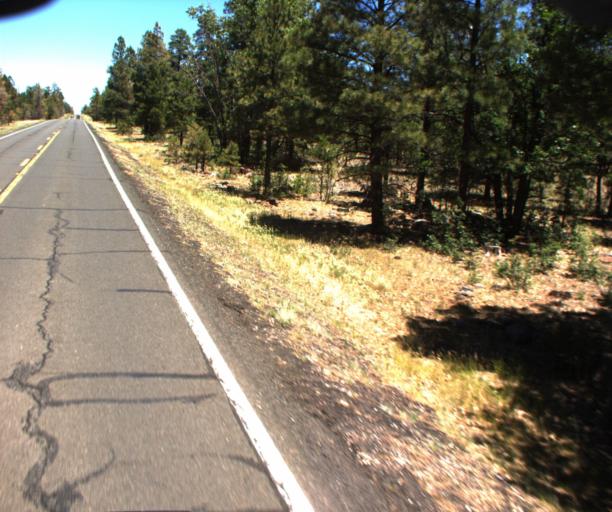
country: US
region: Arizona
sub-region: Gila County
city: Pine
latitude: 34.5788
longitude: -111.2635
